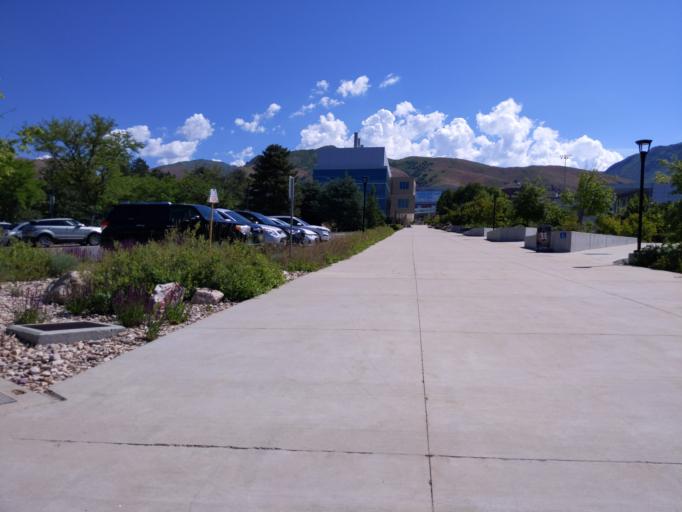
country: US
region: Utah
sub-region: Salt Lake County
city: Salt Lake City
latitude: 40.7673
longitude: -111.8442
